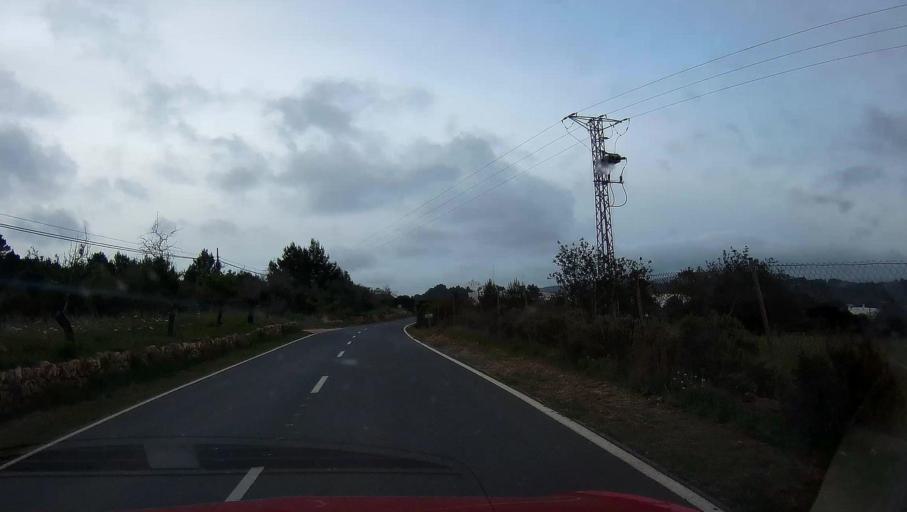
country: ES
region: Balearic Islands
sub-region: Illes Balears
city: Sant Joan de Labritja
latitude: 39.0511
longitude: 1.4334
